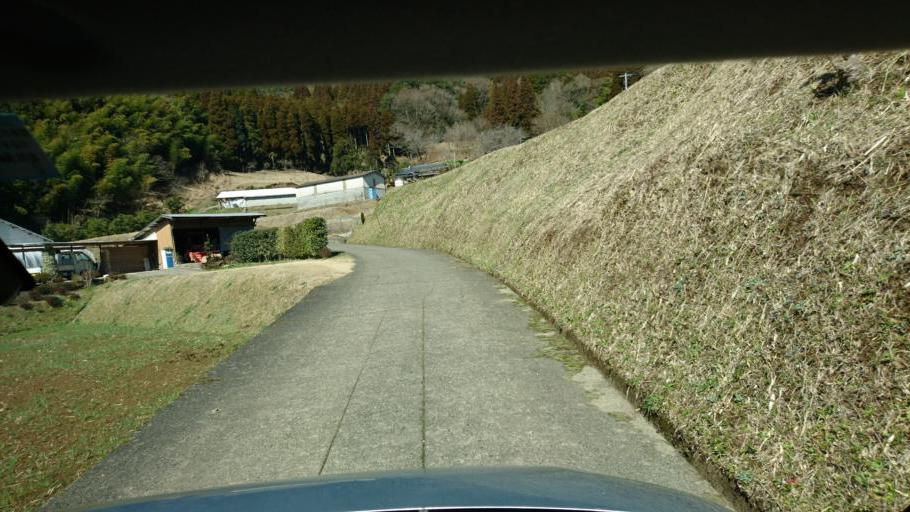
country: JP
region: Oita
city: Takedamachi
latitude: 32.7246
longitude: 131.3082
